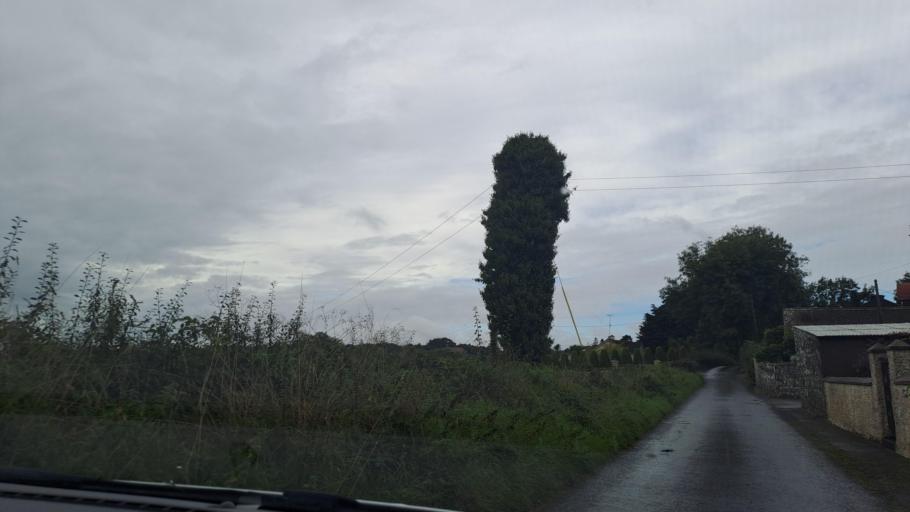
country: IE
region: Ulster
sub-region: County Monaghan
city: Carrickmacross
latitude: 53.9826
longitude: -6.7771
